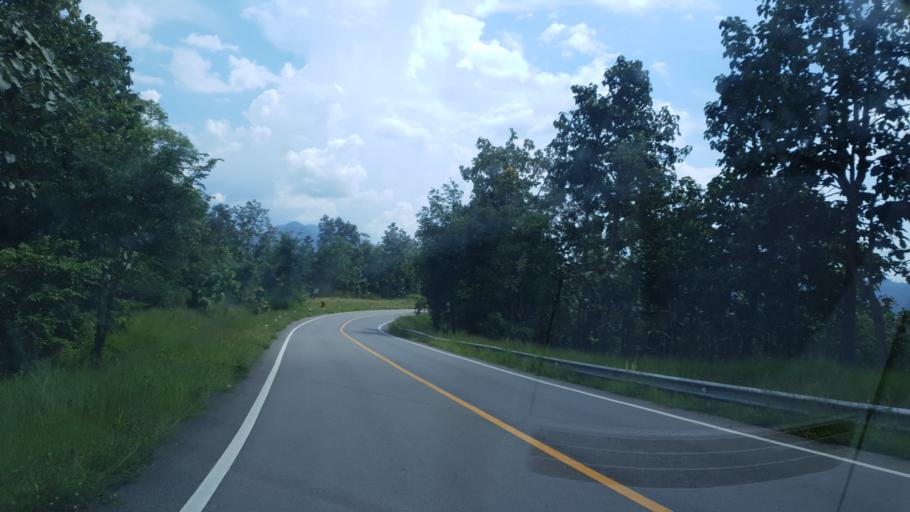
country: TH
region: Mae Hong Son
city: Khun Yuam
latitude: 18.7525
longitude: 97.9271
